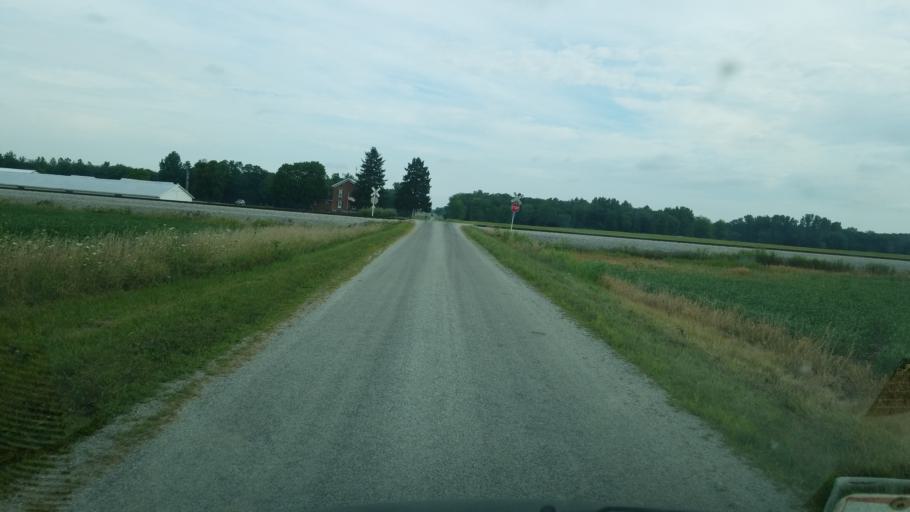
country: US
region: Ohio
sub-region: Crawford County
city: Bucyrus
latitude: 40.9571
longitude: -83.0550
